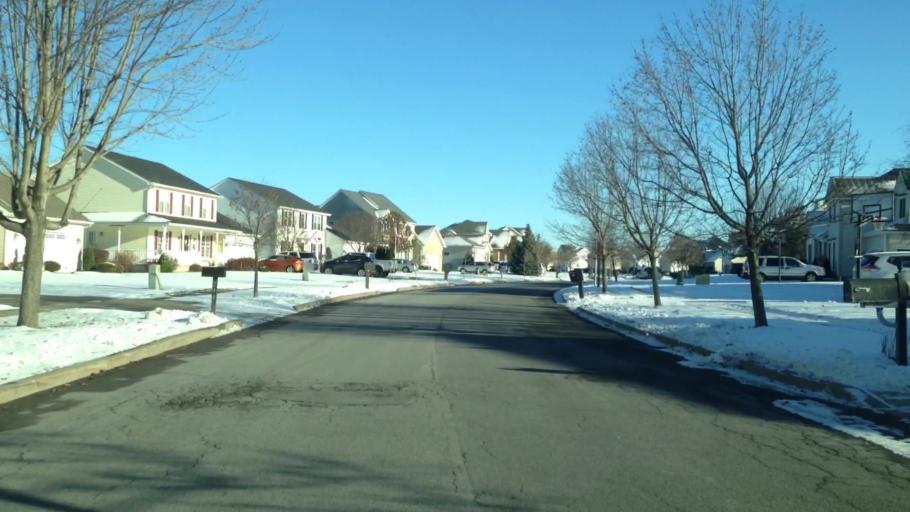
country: US
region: New York
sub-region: Erie County
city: Depew
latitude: 42.8673
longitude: -78.6870
